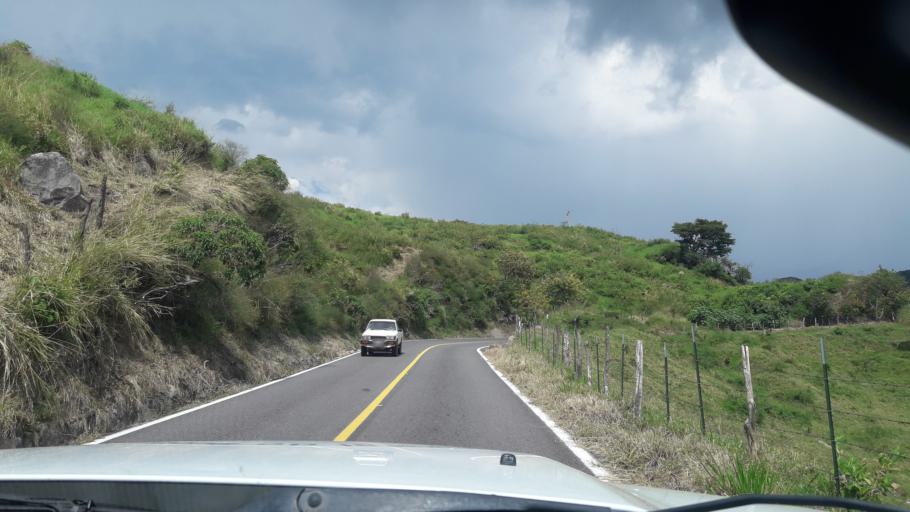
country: MX
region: Colima
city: Suchitlan
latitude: 19.4354
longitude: -103.7115
